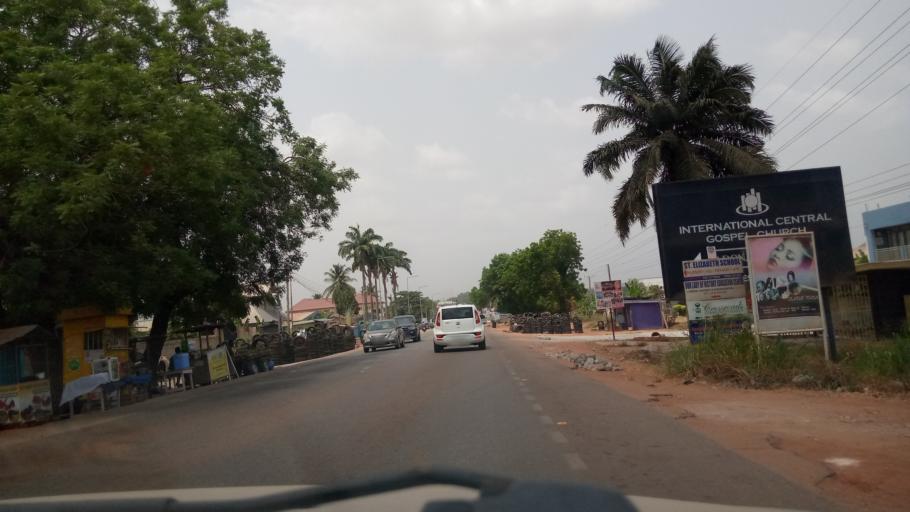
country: GH
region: Greater Accra
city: Dome
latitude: 5.6675
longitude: -0.2090
